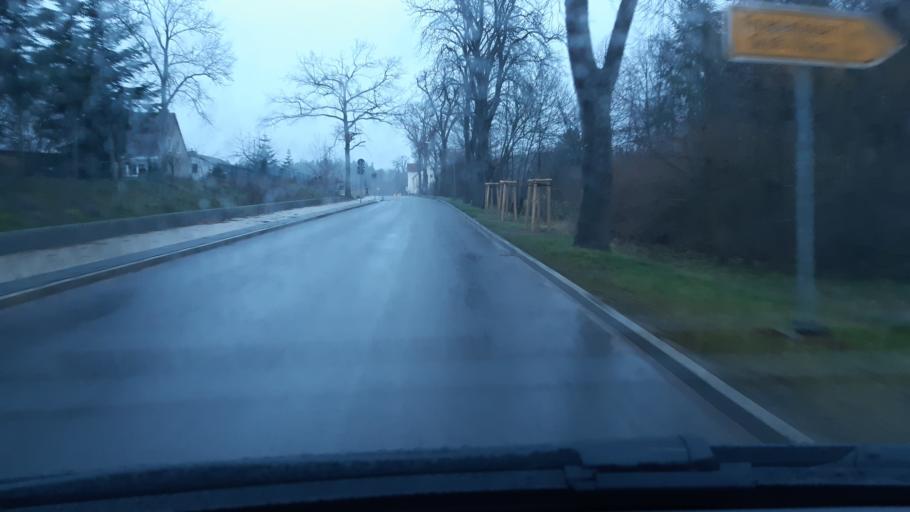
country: DE
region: Brandenburg
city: Milmersdorf
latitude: 53.1144
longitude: 13.6416
